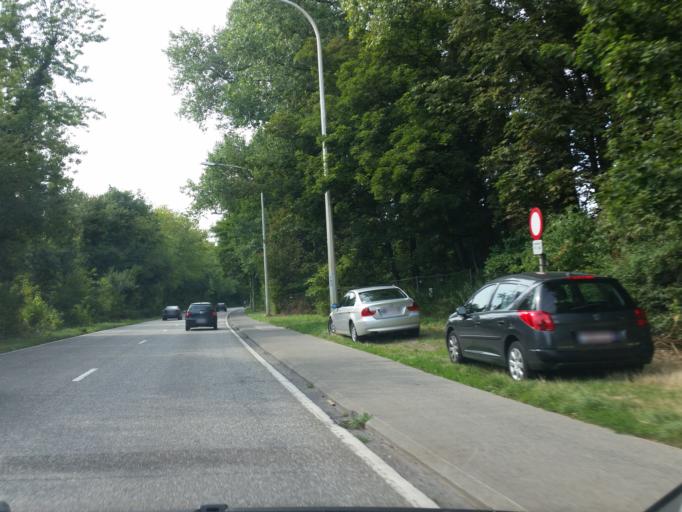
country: BE
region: Flanders
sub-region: Provincie Vlaams-Brabant
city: Diegem
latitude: 50.8978
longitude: 4.4307
